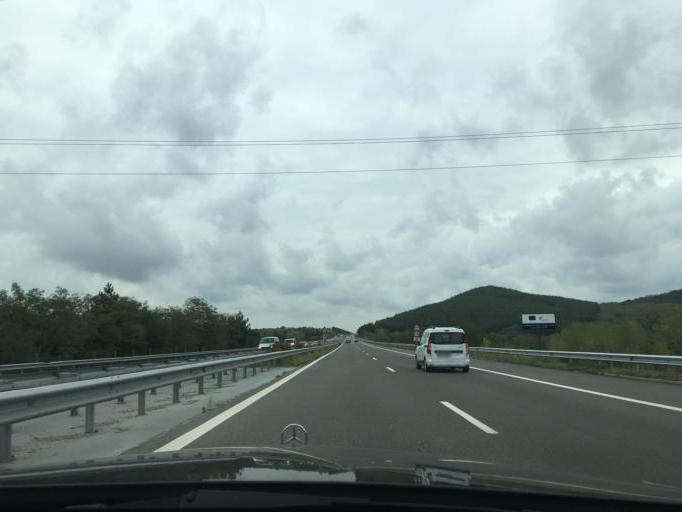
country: BG
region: Pazardzhik
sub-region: Obshtina Lesichevo
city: Lesichevo
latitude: 42.3414
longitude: 24.0541
